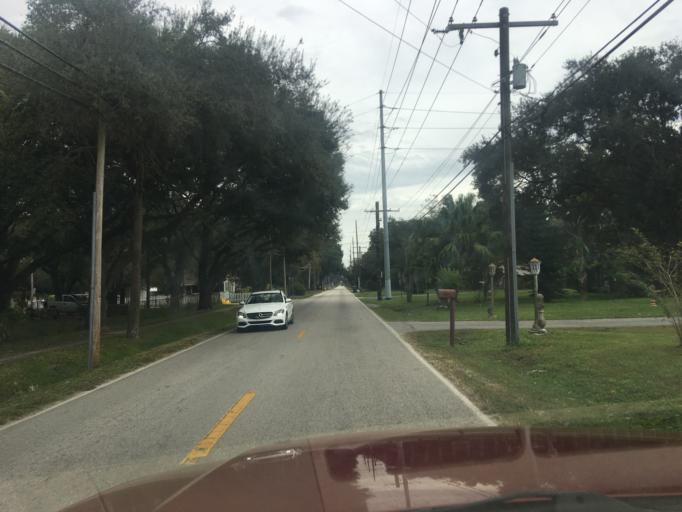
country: US
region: Florida
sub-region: Hillsborough County
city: Gibsonton
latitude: 27.8461
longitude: -82.3715
